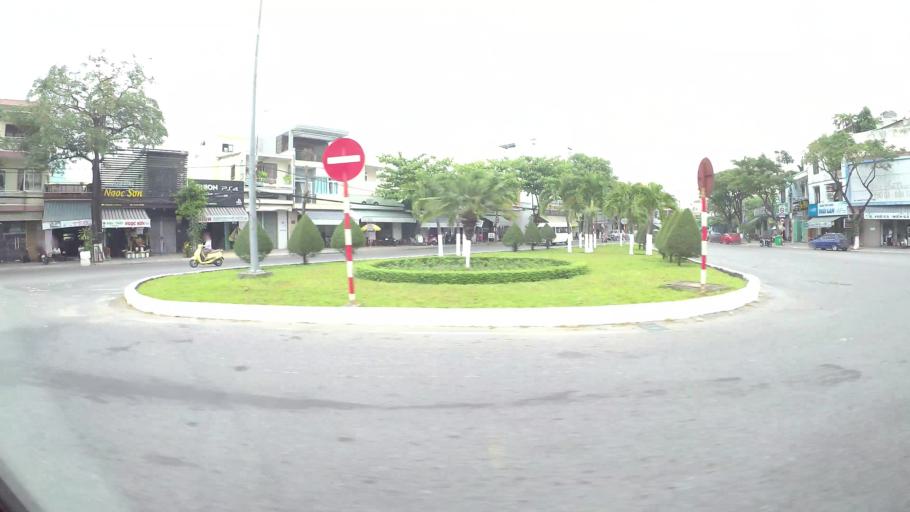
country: VN
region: Da Nang
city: Da Nang
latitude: 16.0564
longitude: 108.2077
